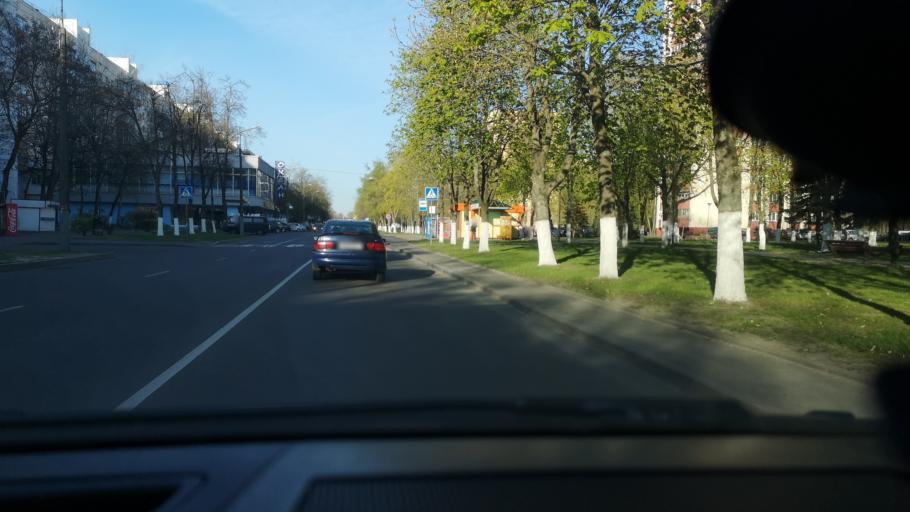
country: BY
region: Gomel
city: Gomel
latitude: 52.4518
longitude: 31.0024
